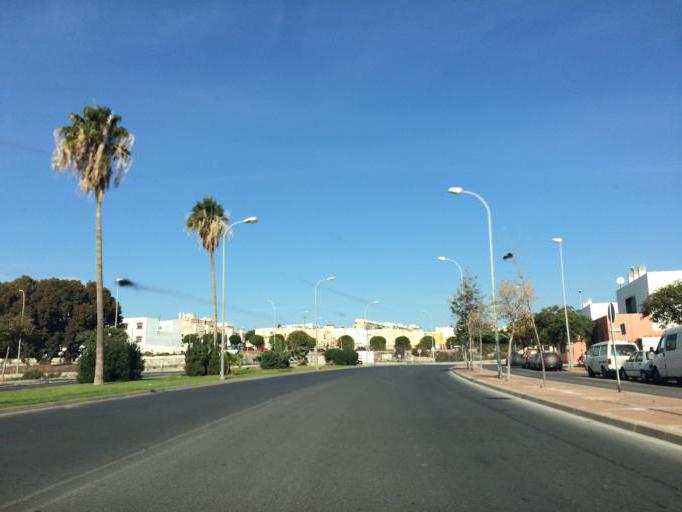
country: ES
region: Andalusia
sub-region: Provincia de Almeria
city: Almeria
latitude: 36.8470
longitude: -2.4342
